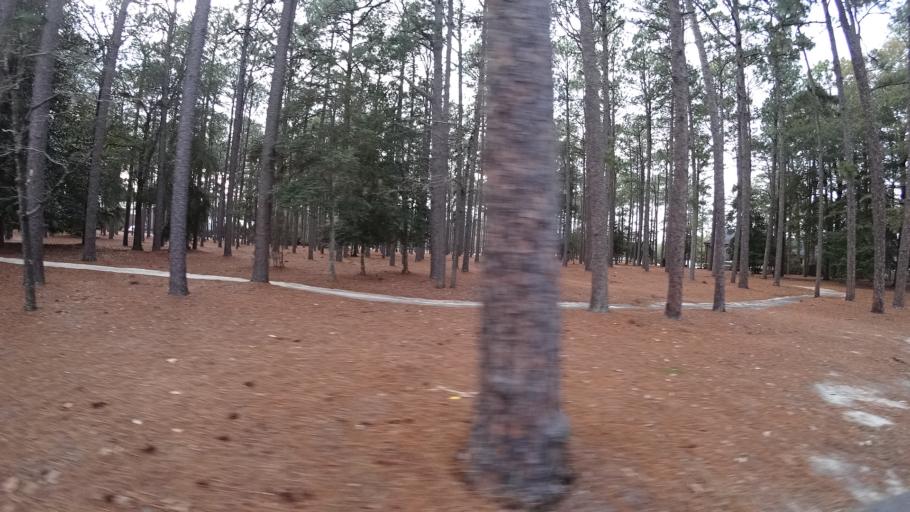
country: US
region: North Carolina
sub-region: Moore County
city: Pinehurst
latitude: 35.1948
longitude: -79.4667
